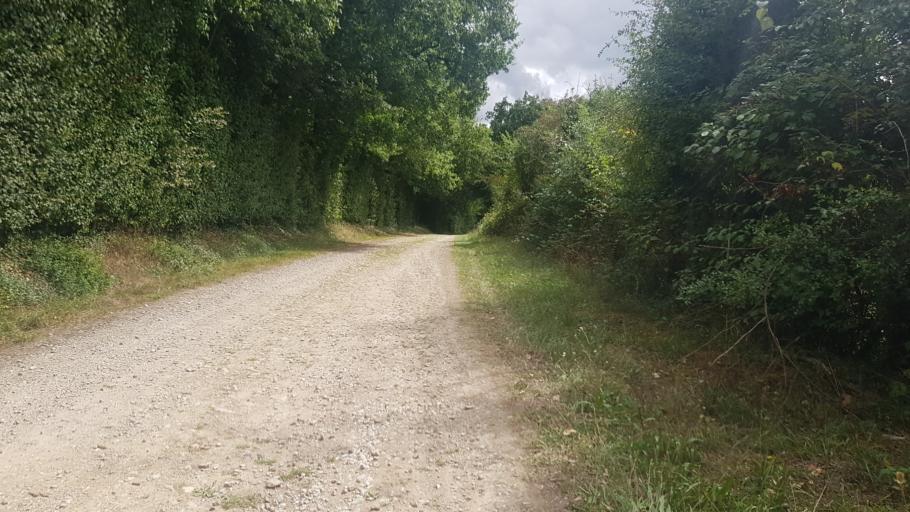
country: FR
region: Poitou-Charentes
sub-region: Departement des Deux-Sevres
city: Vouille
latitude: 46.3169
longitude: -0.3432
